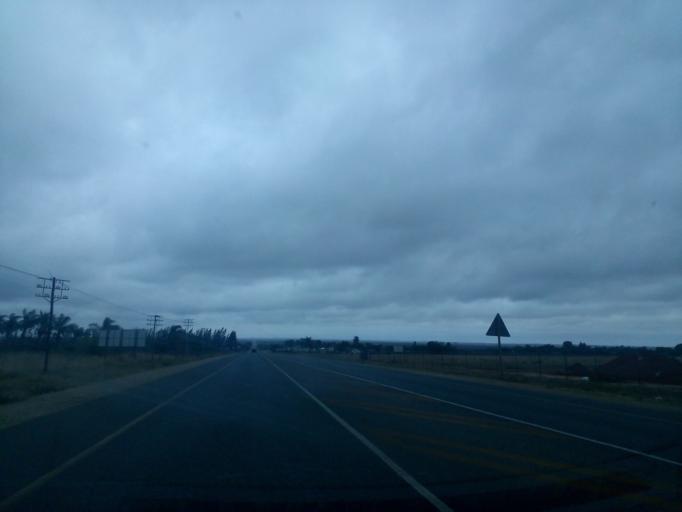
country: ZA
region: Limpopo
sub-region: Vhembe District Municipality
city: Louis Trichardt
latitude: -23.0719
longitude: 29.9109
